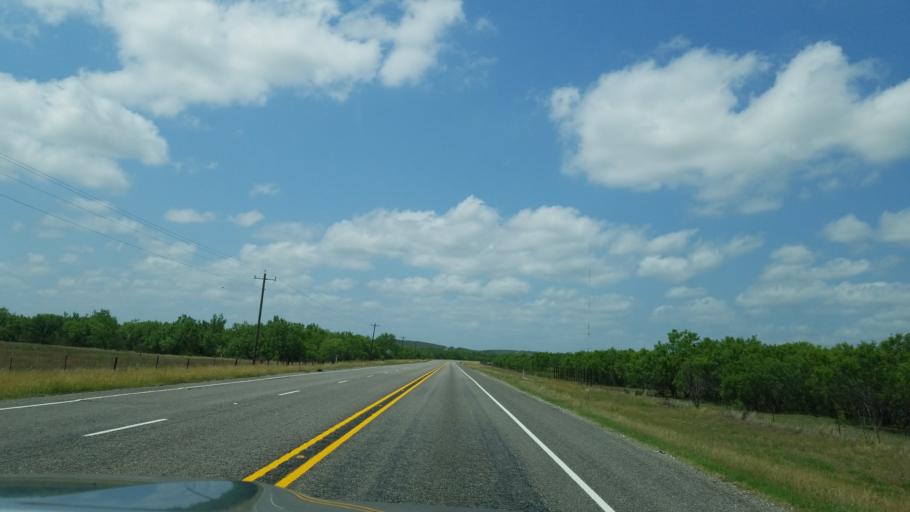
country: US
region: Texas
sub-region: Frio County
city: Pearsall
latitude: 28.9513
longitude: -99.2666
